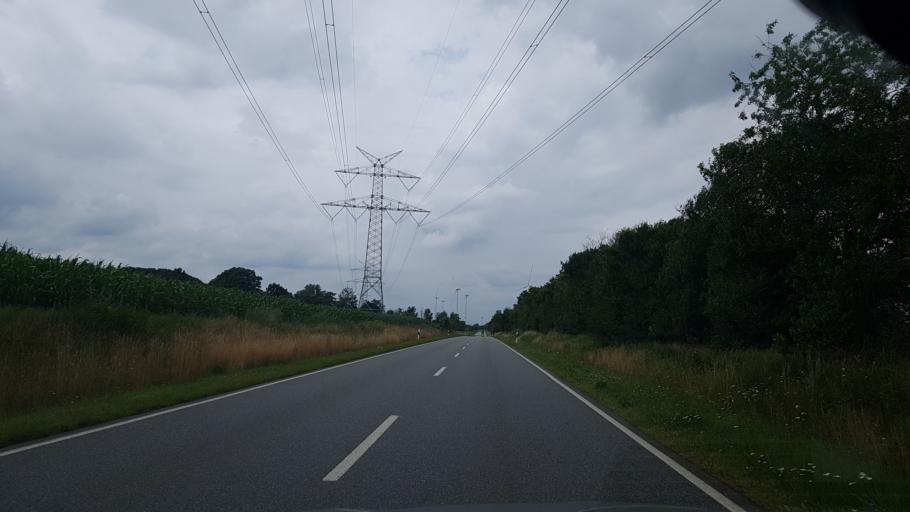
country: DE
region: Schleswig-Holstein
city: Jardelund
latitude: 54.8312
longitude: 9.2161
